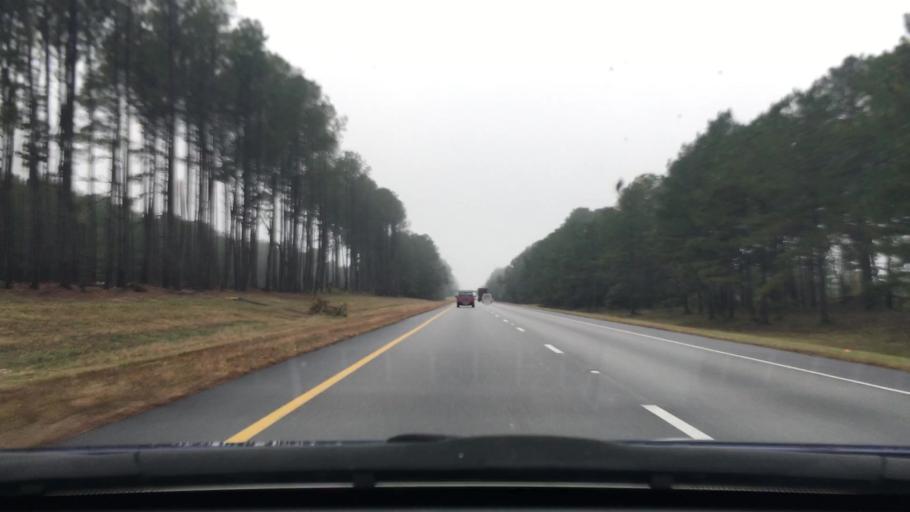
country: US
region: South Carolina
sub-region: Lee County
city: Bishopville
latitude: 34.2029
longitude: -80.3638
